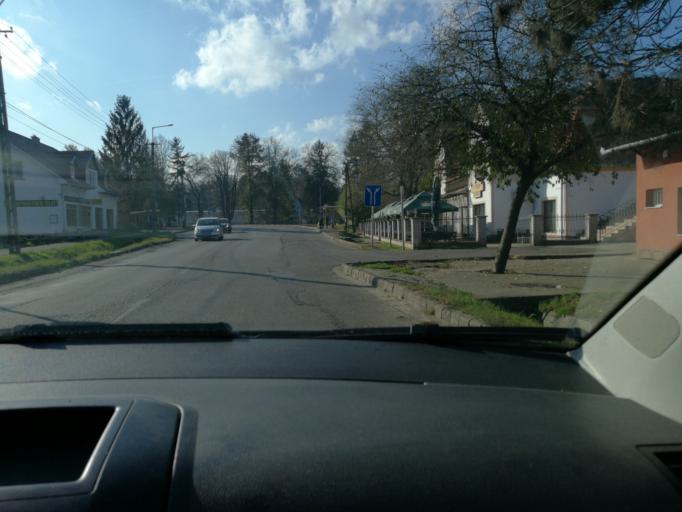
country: HU
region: Nograd
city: Batonyterenye
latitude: 47.9782
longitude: 19.8210
